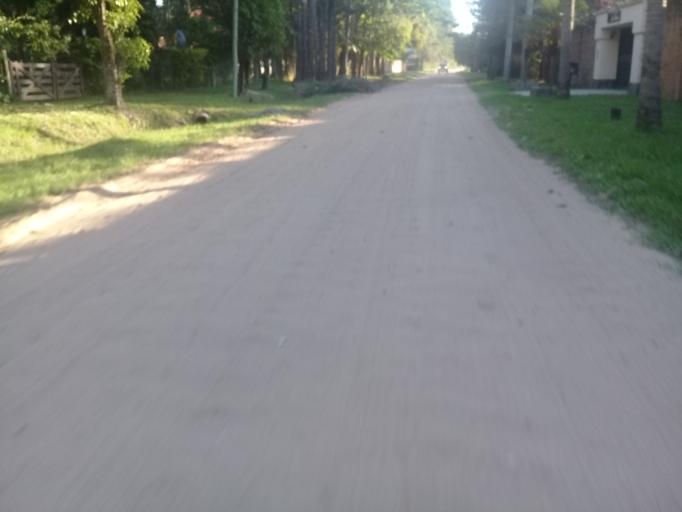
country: AR
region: Corrientes
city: San Luis del Palmar
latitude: -27.4628
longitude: -58.6658
